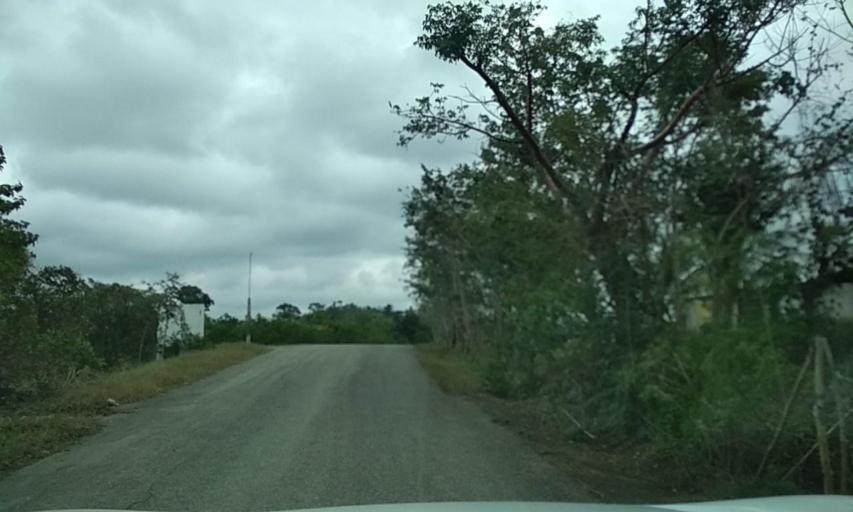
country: MX
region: Veracruz
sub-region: Coatzintla
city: Manuel Maria Contreras
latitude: 20.3408
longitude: -97.4633
